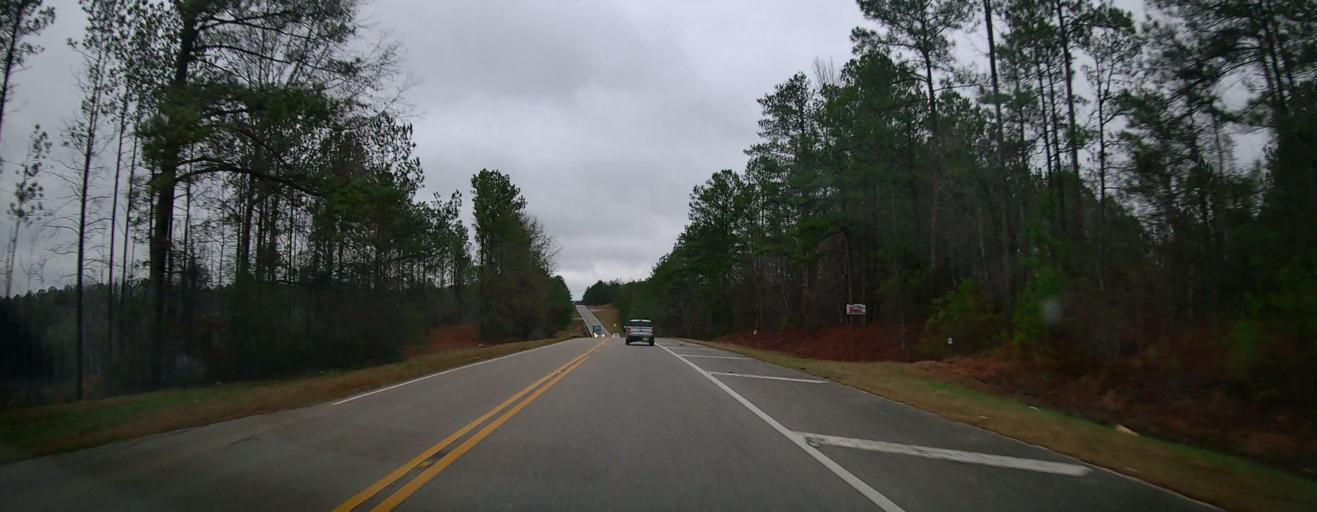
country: US
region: Alabama
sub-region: Bibb County
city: Centreville
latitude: 32.8598
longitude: -86.9670
